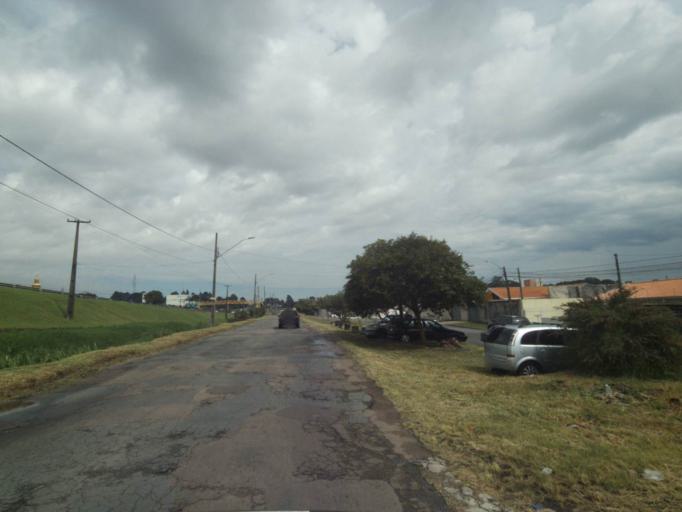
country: BR
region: Parana
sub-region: Pinhais
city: Pinhais
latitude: -25.4788
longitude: -49.2007
